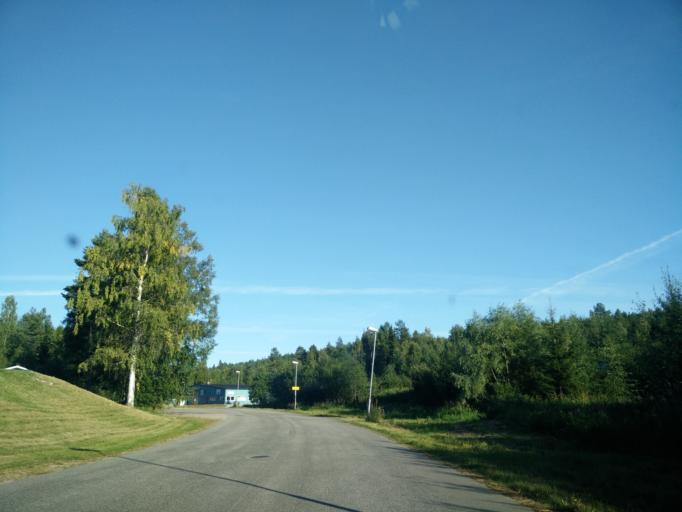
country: SE
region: Vaesternorrland
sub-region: Sundsvalls Kommun
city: Sundsvall
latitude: 62.4068
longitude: 17.2862
